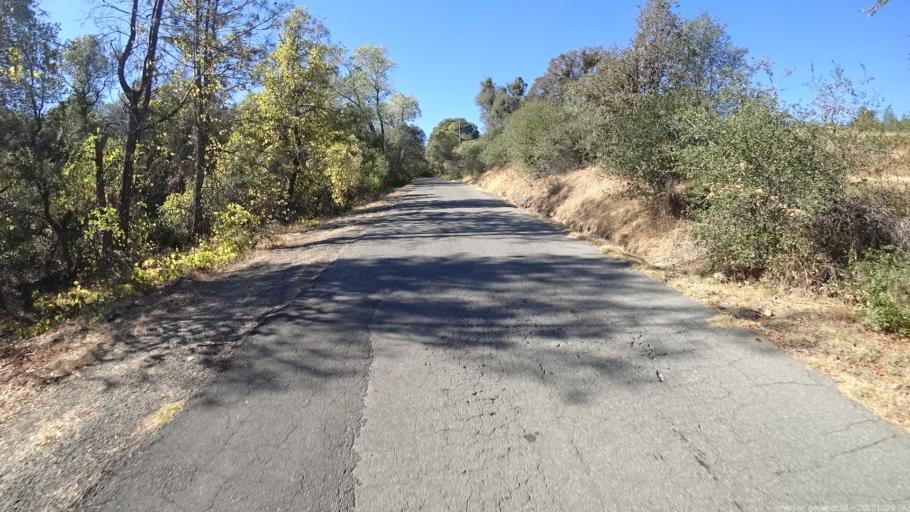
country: US
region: California
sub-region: Shasta County
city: Shasta
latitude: 40.4821
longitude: -122.6688
